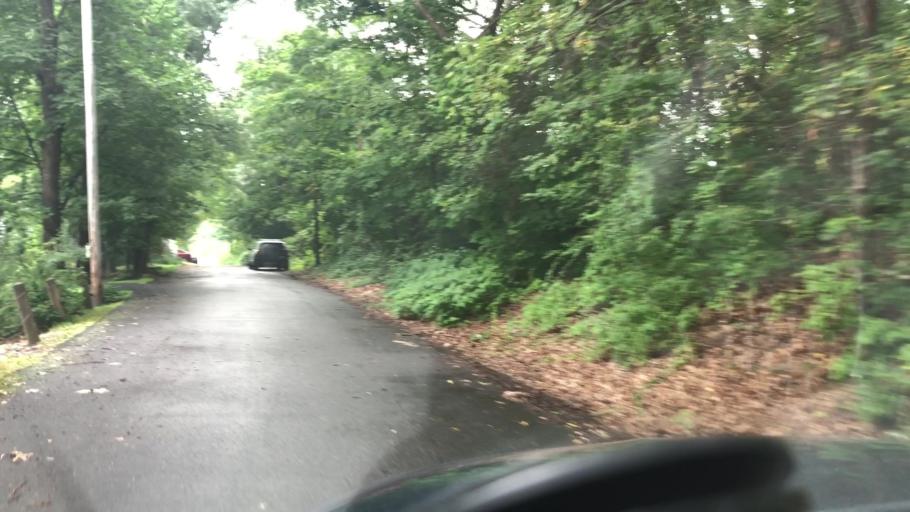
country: US
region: Massachusetts
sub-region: Hampden County
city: Holyoke
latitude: 42.2065
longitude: -72.6361
